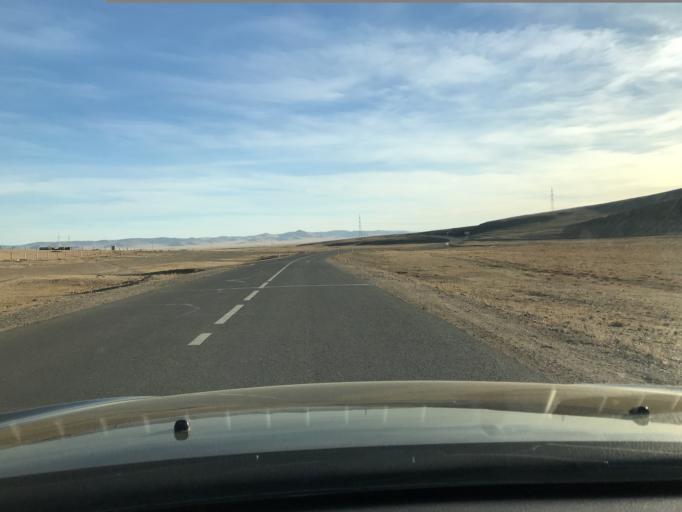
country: MN
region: Central Aimak
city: Dzuunmod
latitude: 47.7986
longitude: 107.3239
